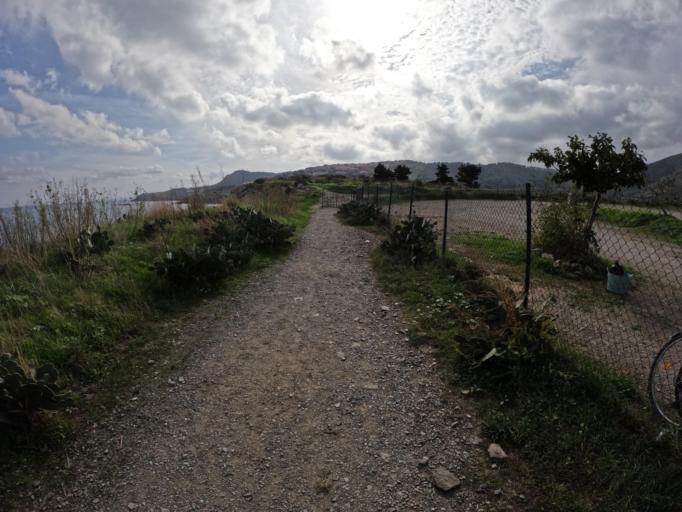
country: FR
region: Languedoc-Roussillon
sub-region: Departement des Pyrenees-Orientales
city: Cervera de la Marenda
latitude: 42.4549
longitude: 3.1648
